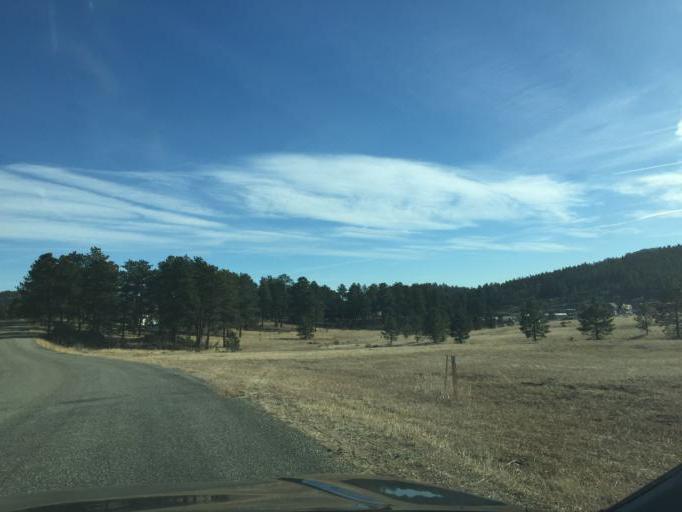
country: US
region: Colorado
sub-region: Jefferson County
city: Evergreen
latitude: 39.4424
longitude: -105.4575
